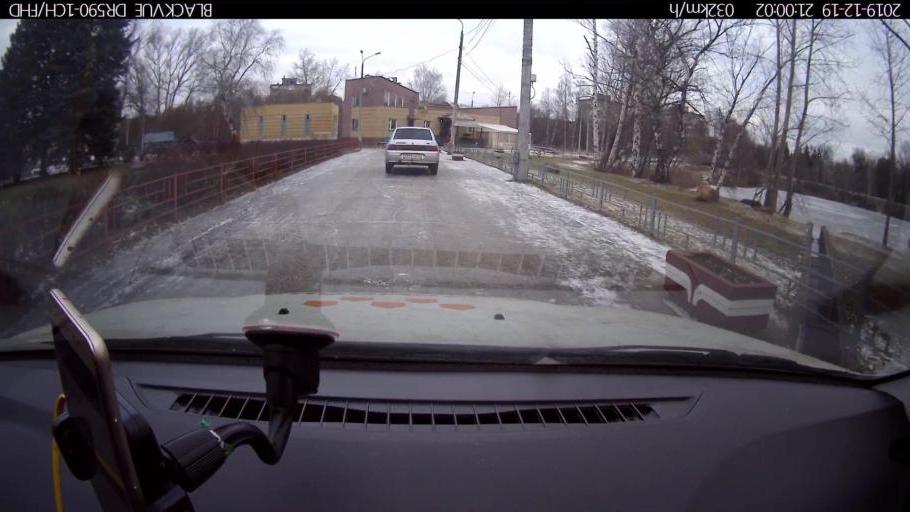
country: RU
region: Nizjnij Novgorod
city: Neklyudovo
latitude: 56.3436
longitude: 43.8564
